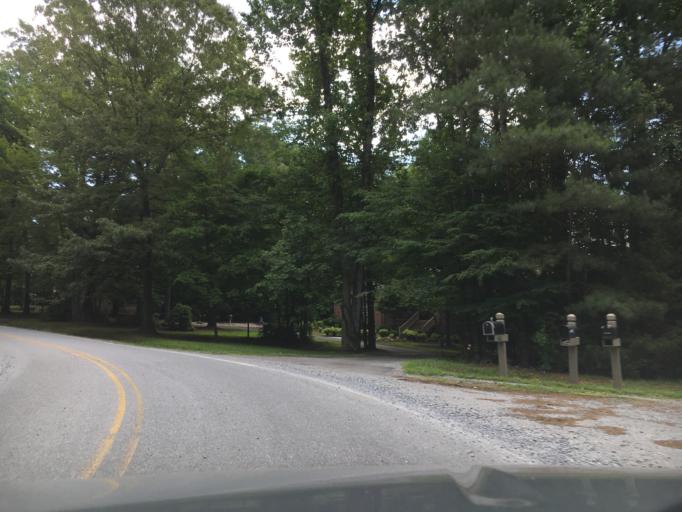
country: US
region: Virginia
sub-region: Bedford County
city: Forest
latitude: 37.3861
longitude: -79.2542
